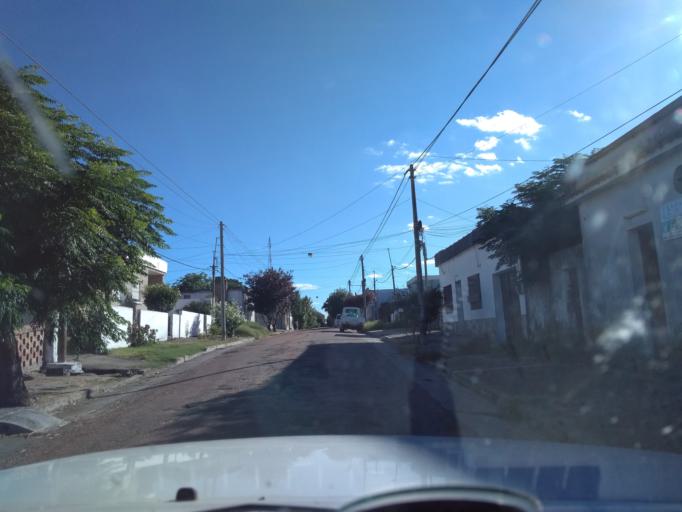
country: UY
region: Florida
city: Florida
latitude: -34.0938
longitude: -56.2089
